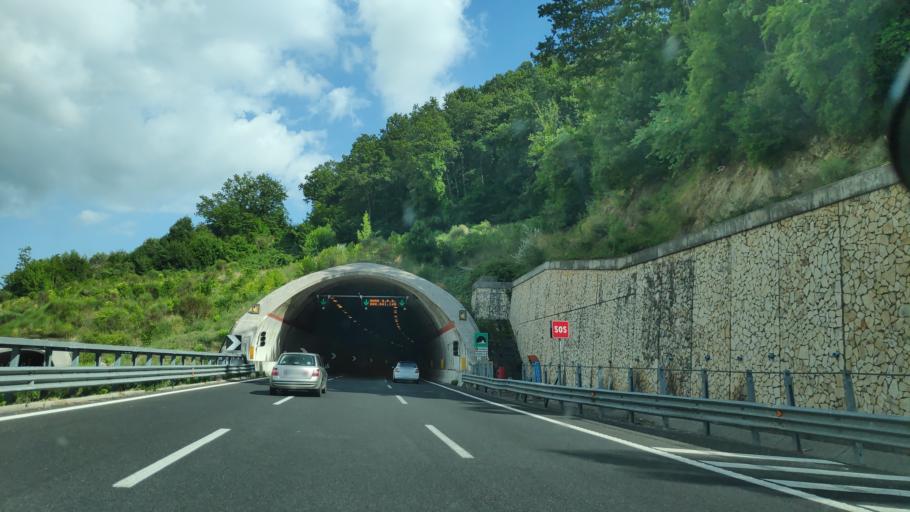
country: IT
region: Campania
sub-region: Provincia di Salerno
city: Contursi Terme
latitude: 40.6266
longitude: 15.2369
